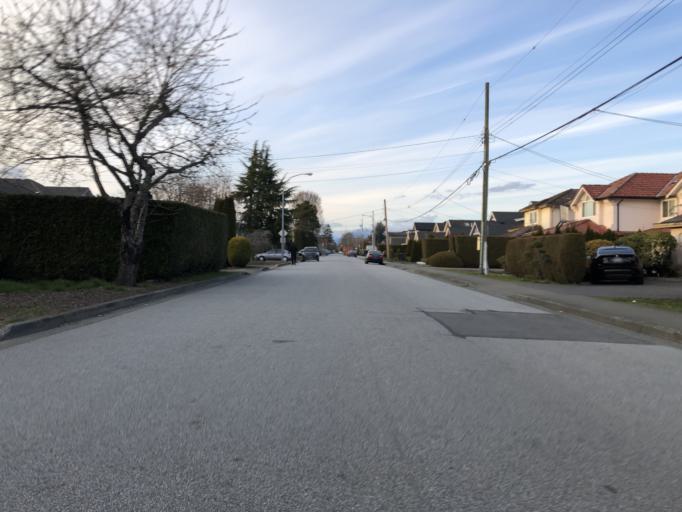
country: CA
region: British Columbia
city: Richmond
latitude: 49.1520
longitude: -123.1198
